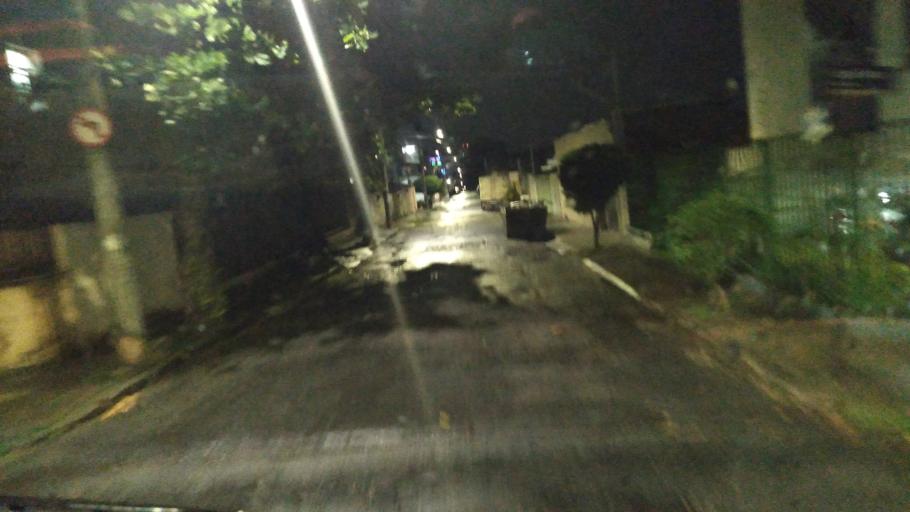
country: BR
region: Minas Gerais
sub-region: Belo Horizonte
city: Belo Horizonte
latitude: -19.9115
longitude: -43.9786
